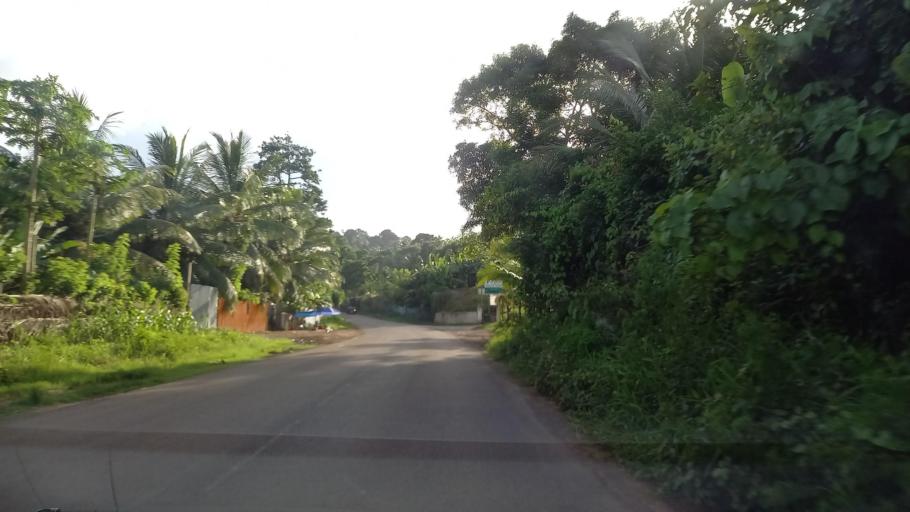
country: YT
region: Bandraboua
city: Bandraboua
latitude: -12.7266
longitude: 45.1217
